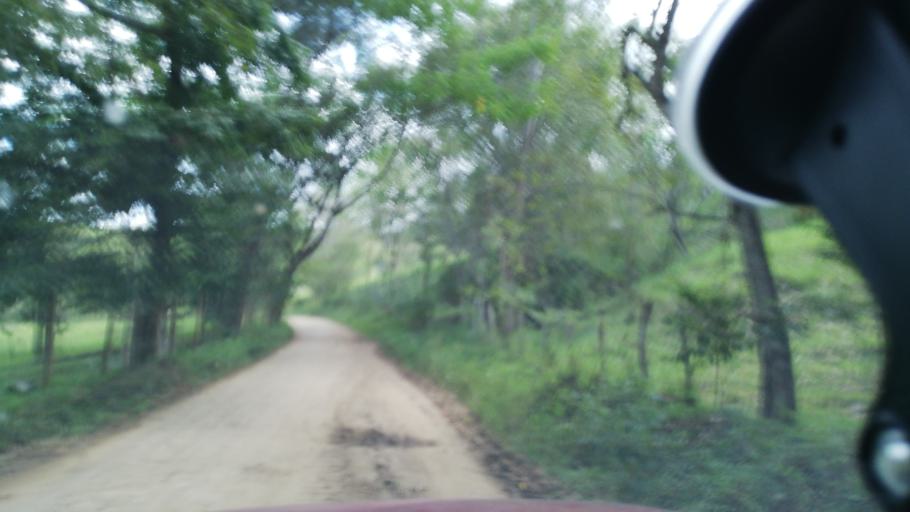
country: CO
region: Cundinamarca
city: Quipile
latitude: 4.8058
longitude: -74.6188
